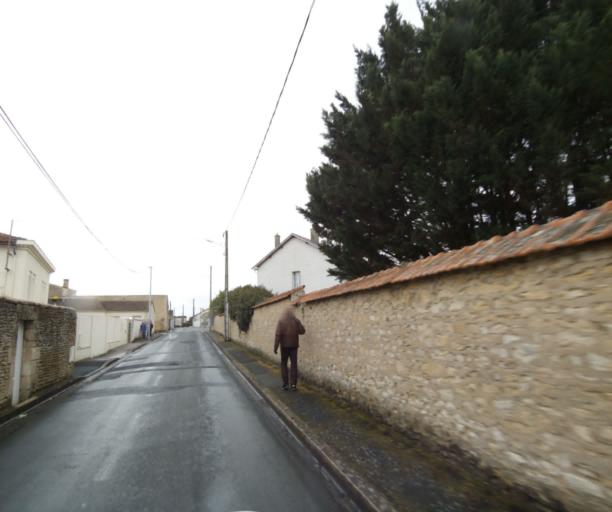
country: FR
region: Poitou-Charentes
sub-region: Departement des Deux-Sevres
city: Niort
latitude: 46.3319
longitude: -0.4465
